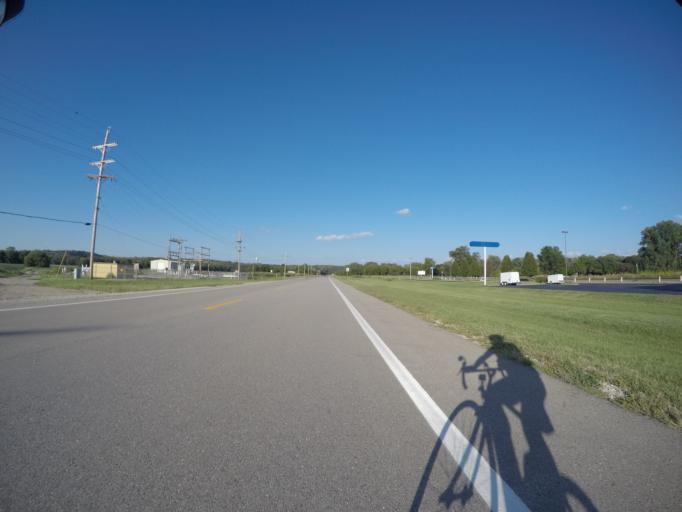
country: US
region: Kansas
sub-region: Riley County
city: Manhattan
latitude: 39.1527
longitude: -96.6400
